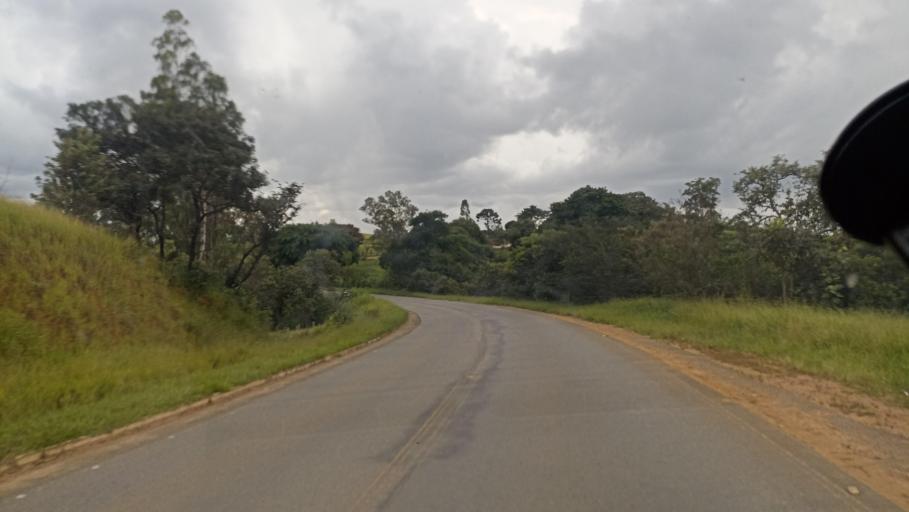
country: BR
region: Minas Gerais
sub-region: Cruzilia
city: Cruzilia
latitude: -21.8955
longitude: -44.8200
